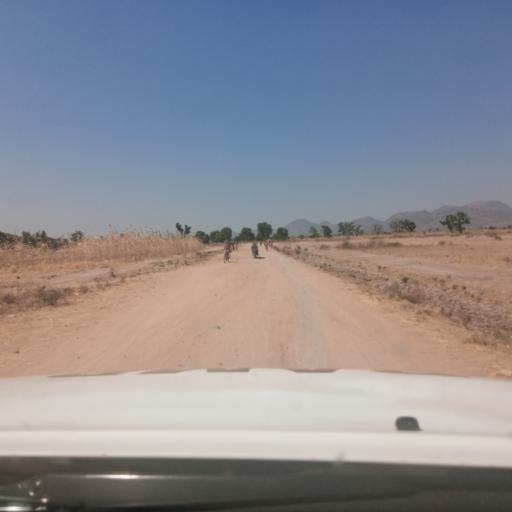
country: NG
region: Adamawa
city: Little Gombi
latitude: 9.7765
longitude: 12.5860
